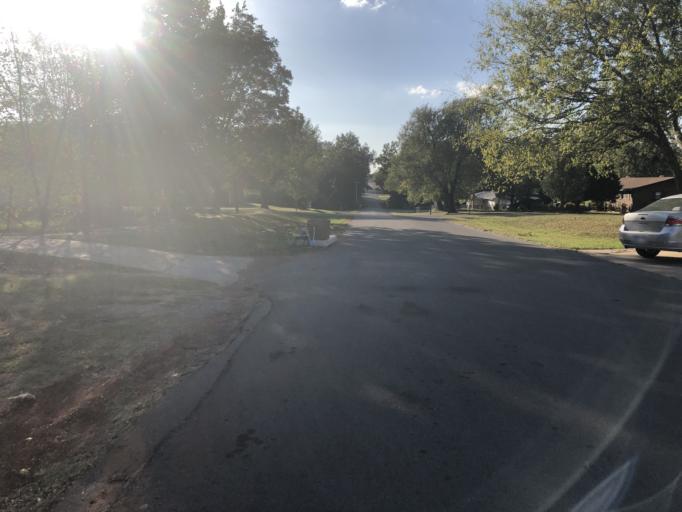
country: US
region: Oklahoma
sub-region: Pottawatomie County
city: Tecumseh
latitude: 35.2587
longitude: -96.9311
